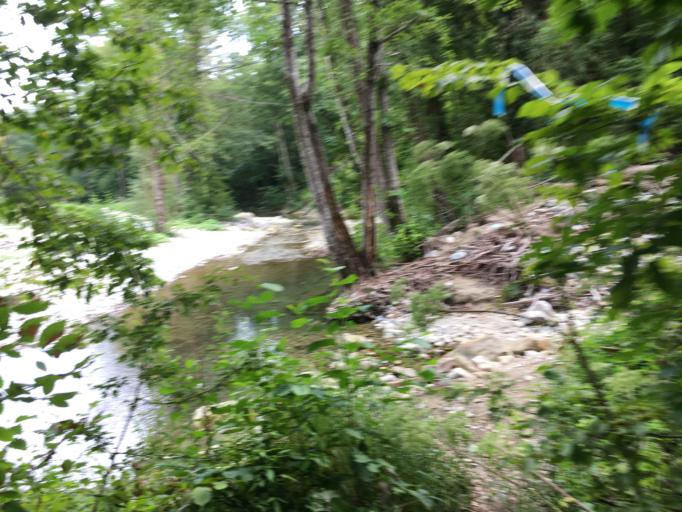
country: RU
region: Krasnodarskiy
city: Tuapse
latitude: 44.2572
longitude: 39.2197
